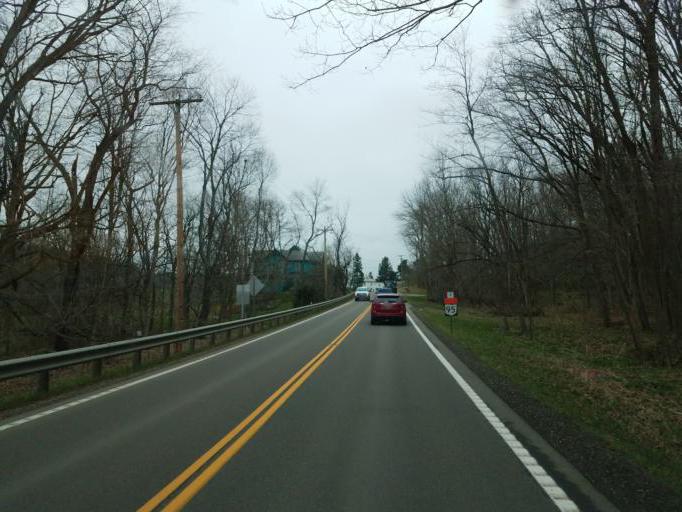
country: US
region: Ohio
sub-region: Ashland County
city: Loudonville
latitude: 40.6697
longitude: -82.2346
